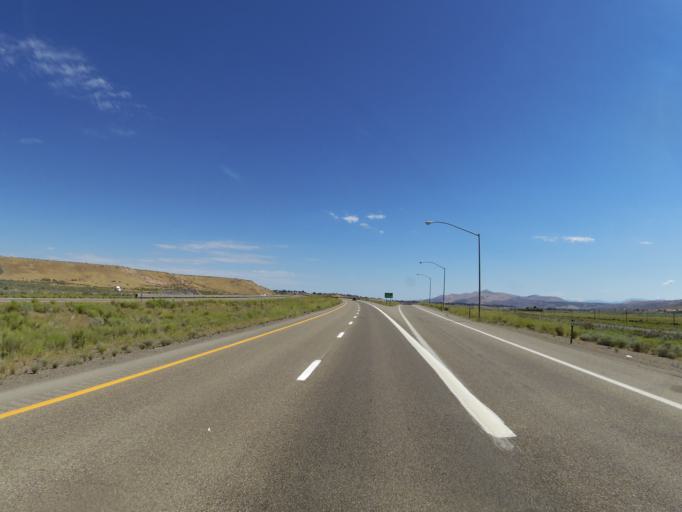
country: US
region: Nevada
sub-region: Elko County
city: Elko
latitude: 40.8056
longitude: -115.8283
